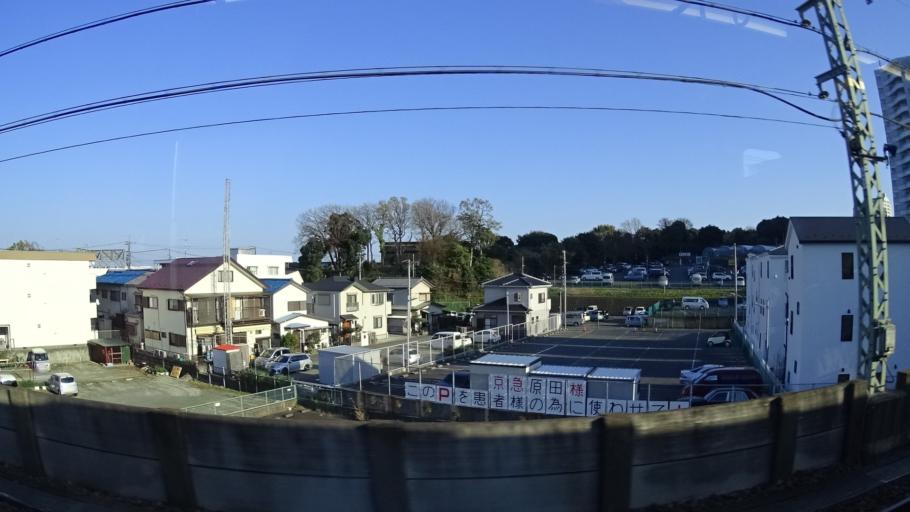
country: JP
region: Kanagawa
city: Miura
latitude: 35.1869
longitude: 139.6515
